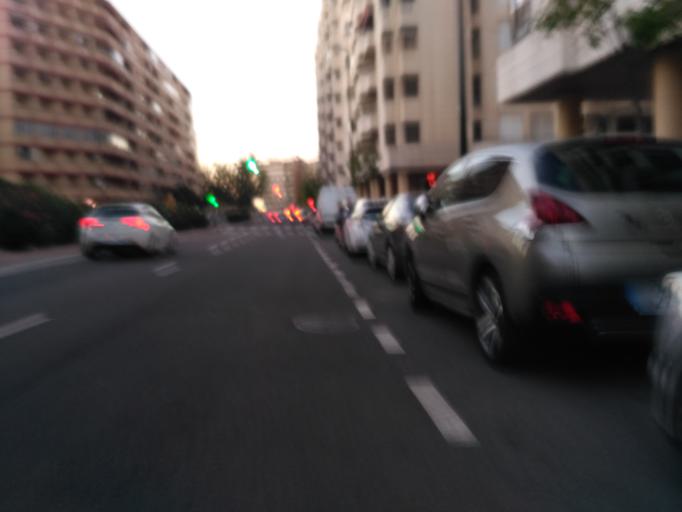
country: ES
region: Aragon
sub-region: Provincia de Zaragoza
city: Almozara
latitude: 41.6522
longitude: -0.8980
